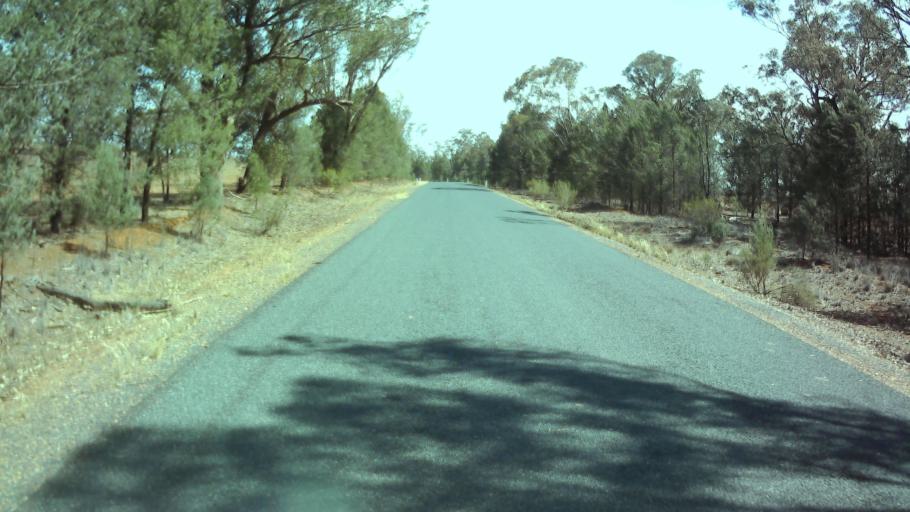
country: AU
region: New South Wales
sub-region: Weddin
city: Grenfell
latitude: -34.0519
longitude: 148.1301
